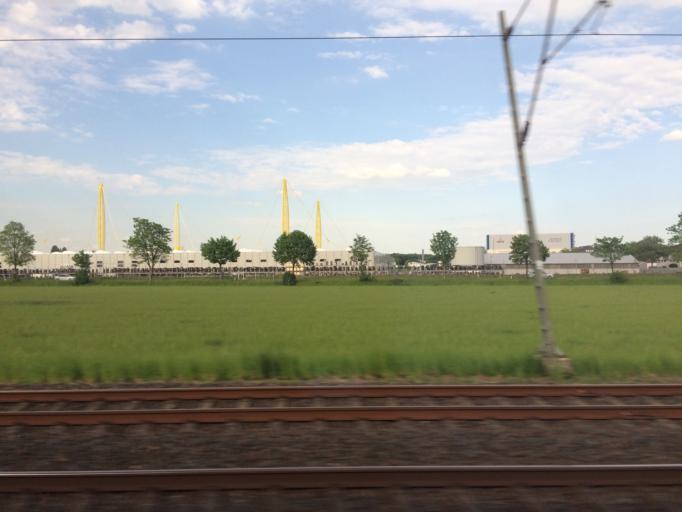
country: DE
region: North Rhine-Westphalia
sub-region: Regierungsbezirk Koln
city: Wahn-Heide
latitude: 50.8396
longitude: 7.0987
